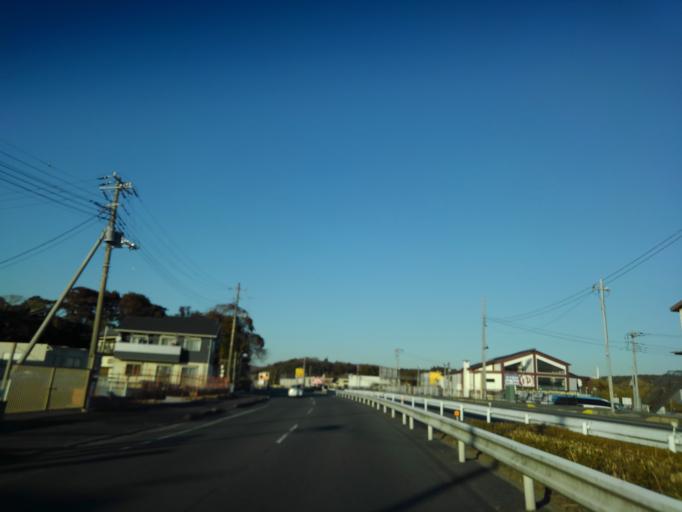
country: JP
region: Chiba
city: Kimitsu
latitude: 35.3135
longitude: 139.9267
